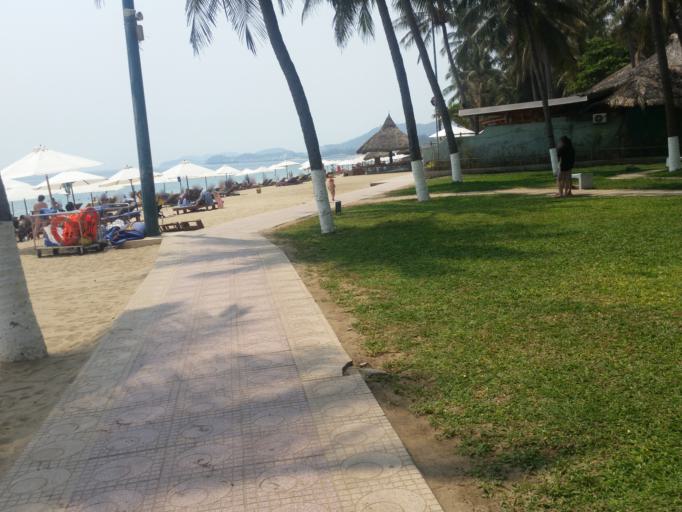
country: VN
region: Khanh Hoa
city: Nha Trang
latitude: 12.2346
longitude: 109.1980
